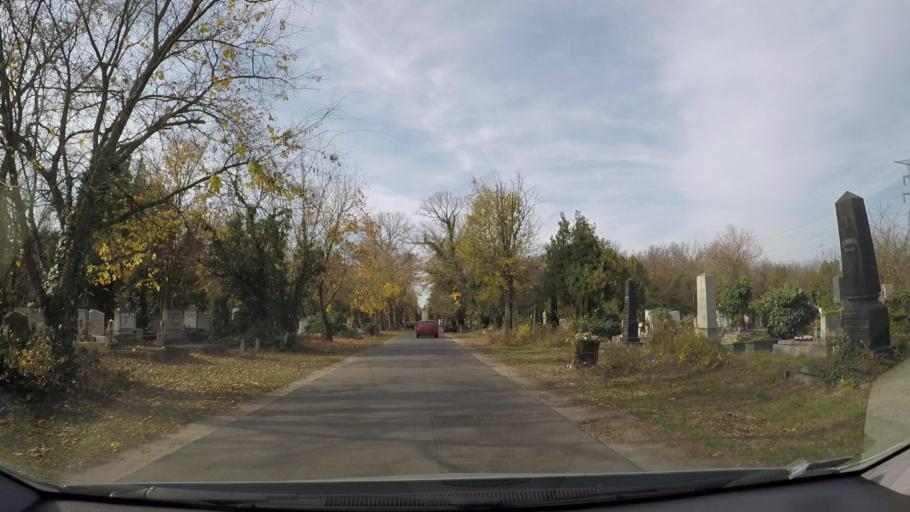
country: HU
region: Budapest
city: Budapest X. keruelet
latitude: 47.4759
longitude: 19.1826
